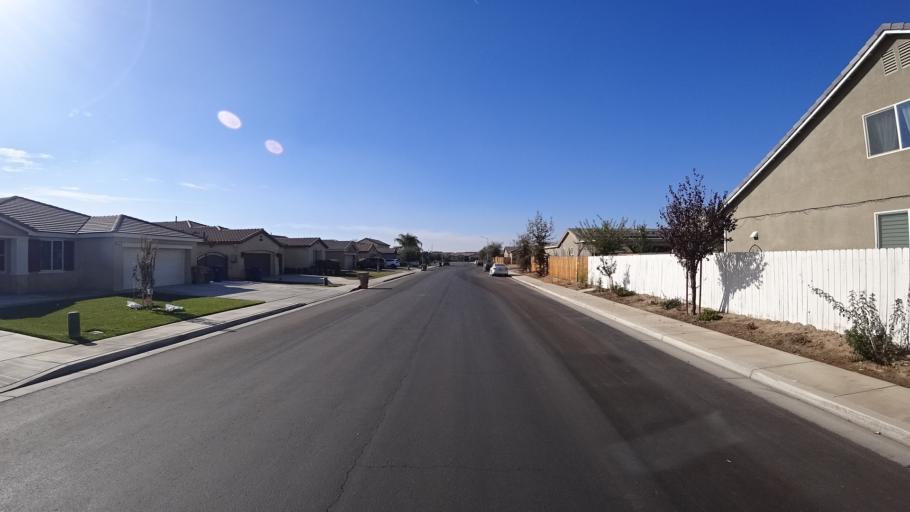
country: US
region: California
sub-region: Kern County
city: Greenfield
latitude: 35.2951
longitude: -119.0630
